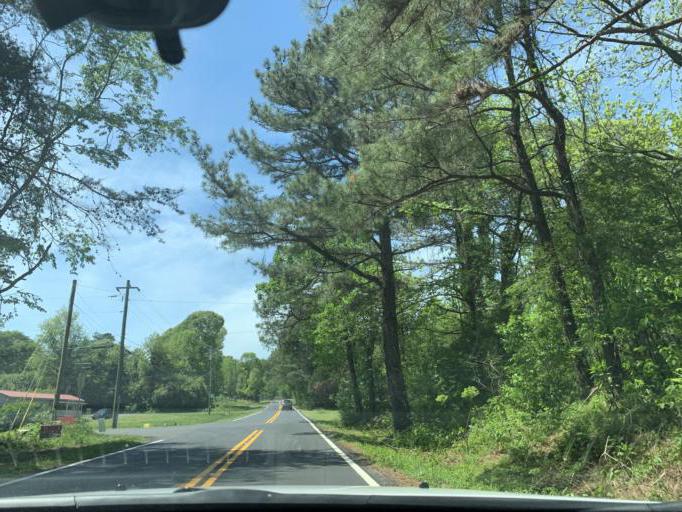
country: US
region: Georgia
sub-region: Forsyth County
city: Cumming
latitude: 34.2635
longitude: -84.0413
